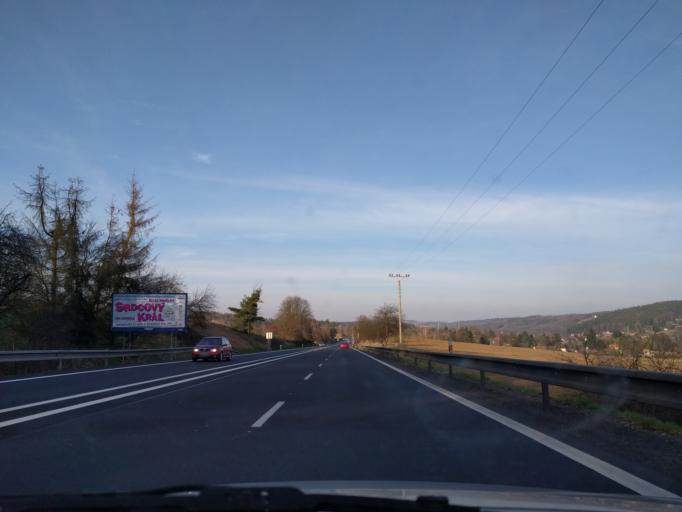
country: CZ
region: Central Bohemia
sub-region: Okres Benesov
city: Cercany
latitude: 49.8572
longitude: 14.6913
